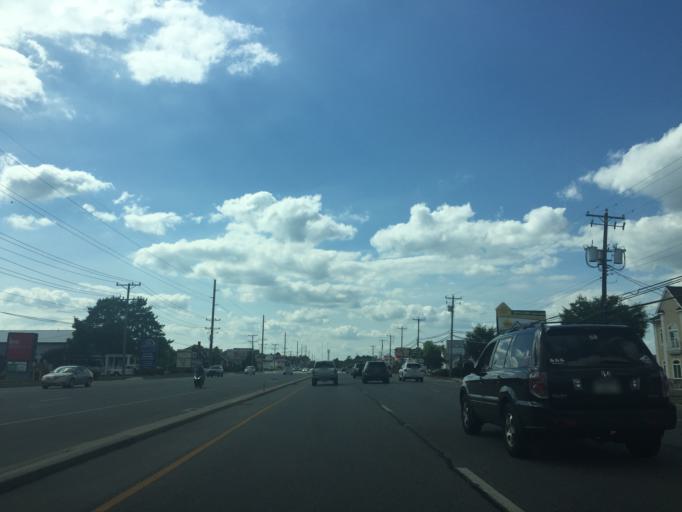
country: US
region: Delaware
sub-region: Sussex County
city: Lewes
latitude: 38.7406
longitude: -75.1470
